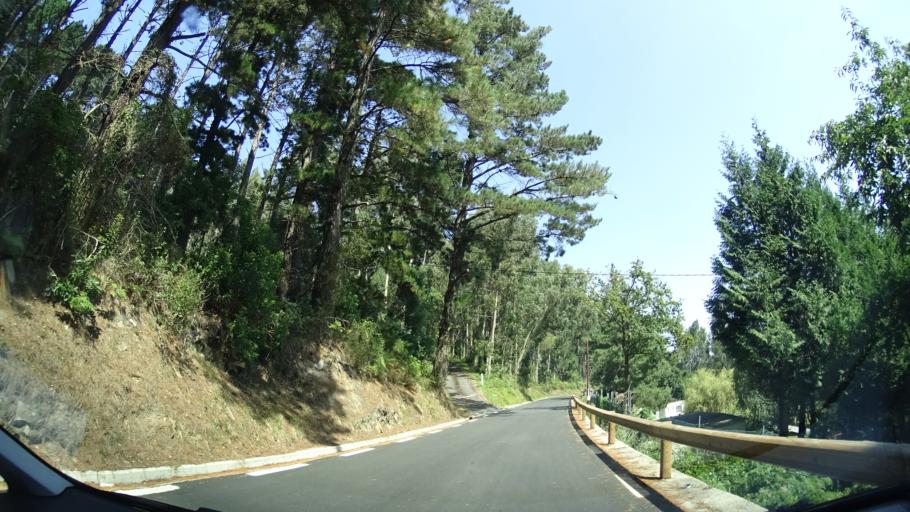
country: ES
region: Basque Country
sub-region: Bizkaia
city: Bermeo
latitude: 43.4428
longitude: -2.7513
